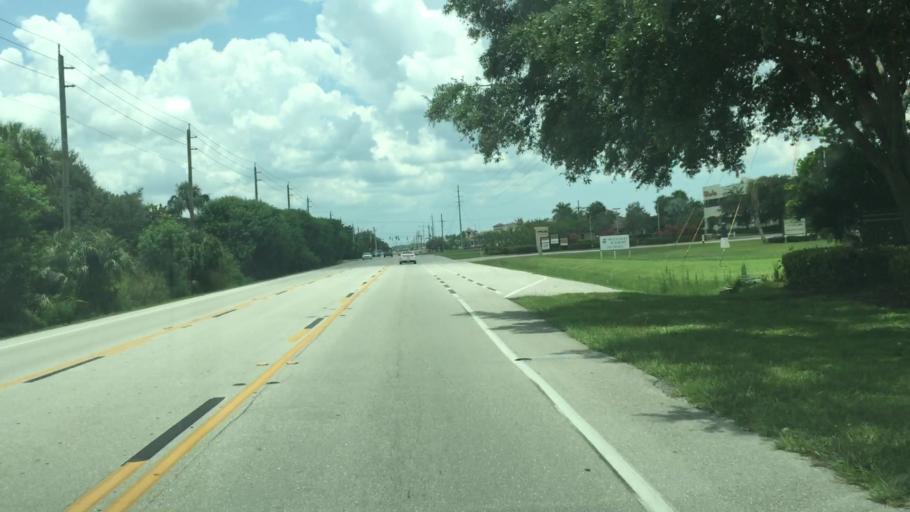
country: US
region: Florida
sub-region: Lee County
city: Villas
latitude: 26.5507
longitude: -81.8468
